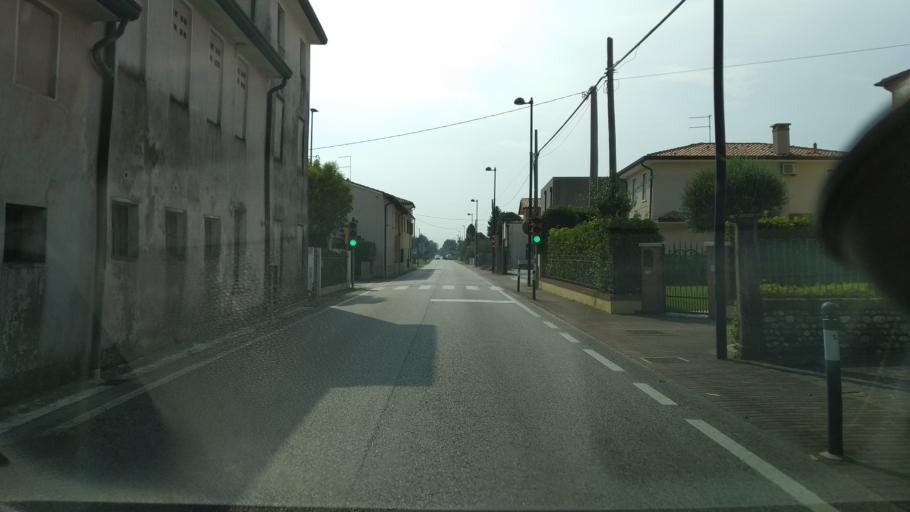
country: IT
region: Veneto
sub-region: Provincia di Padova
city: Cittadella
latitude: 45.6652
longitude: 11.7733
